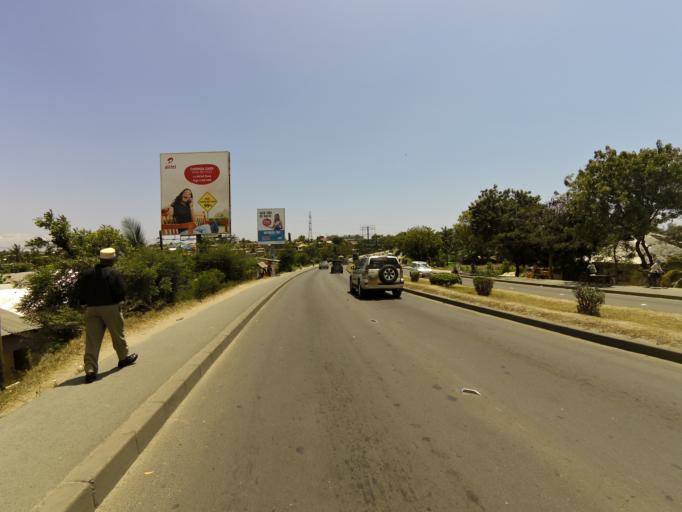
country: TZ
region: Dar es Salaam
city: Magomeni
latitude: -6.8151
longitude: 39.2541
